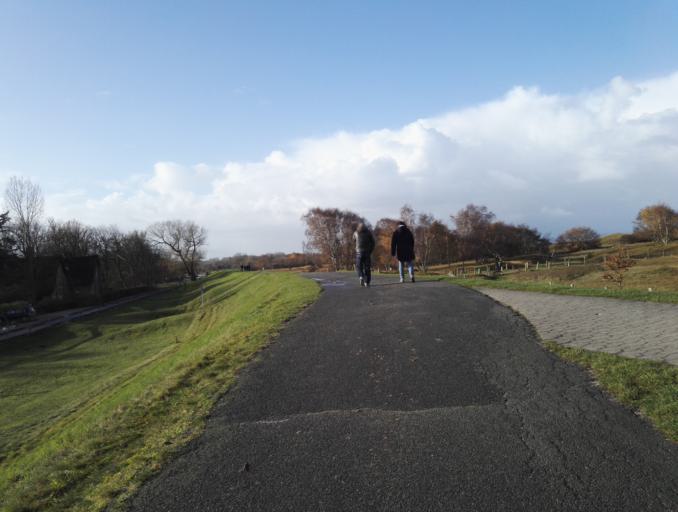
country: DE
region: Schleswig-Holstein
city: Wangels
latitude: 54.3096
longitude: 10.7895
